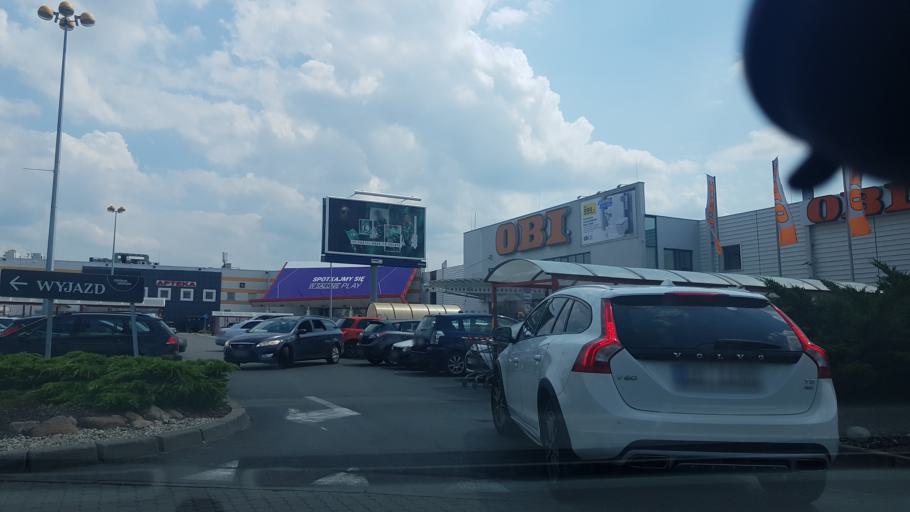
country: PL
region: Masovian Voivodeship
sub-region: Warszawa
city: Ursynow
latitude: 52.1414
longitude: 21.0242
